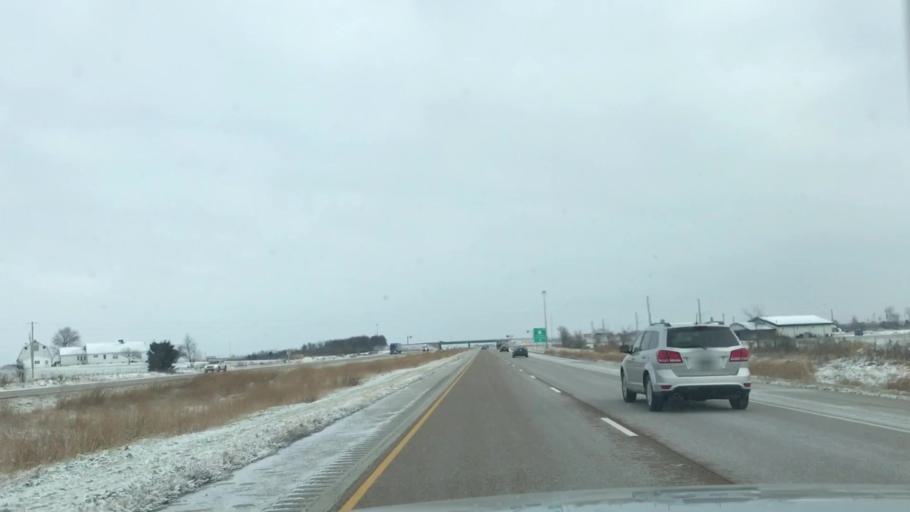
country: US
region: Illinois
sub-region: Montgomery County
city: Litchfield
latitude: 39.1680
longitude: -89.6858
